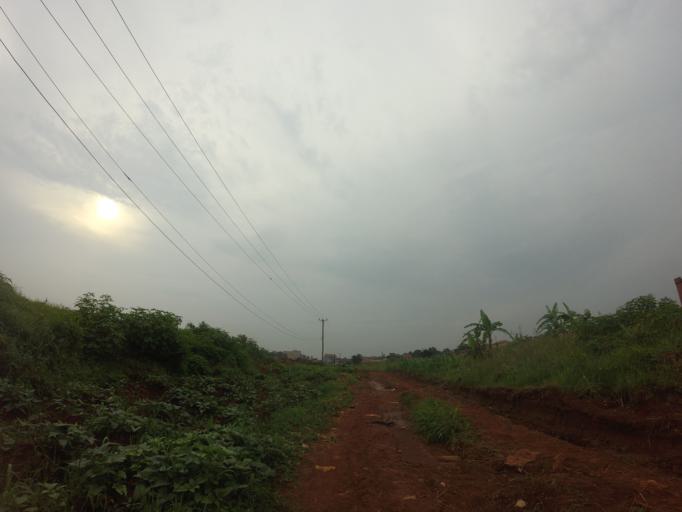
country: UG
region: Central Region
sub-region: Wakiso District
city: Kireka
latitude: 0.3551
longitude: 32.6240
